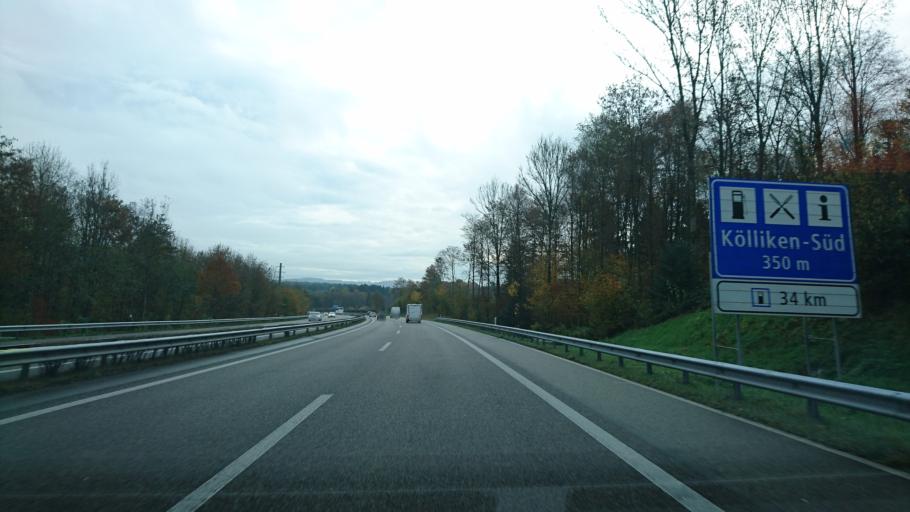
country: CH
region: Aargau
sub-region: Bezirk Zofingen
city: Uerkheim
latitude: 47.3217
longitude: 8.0127
